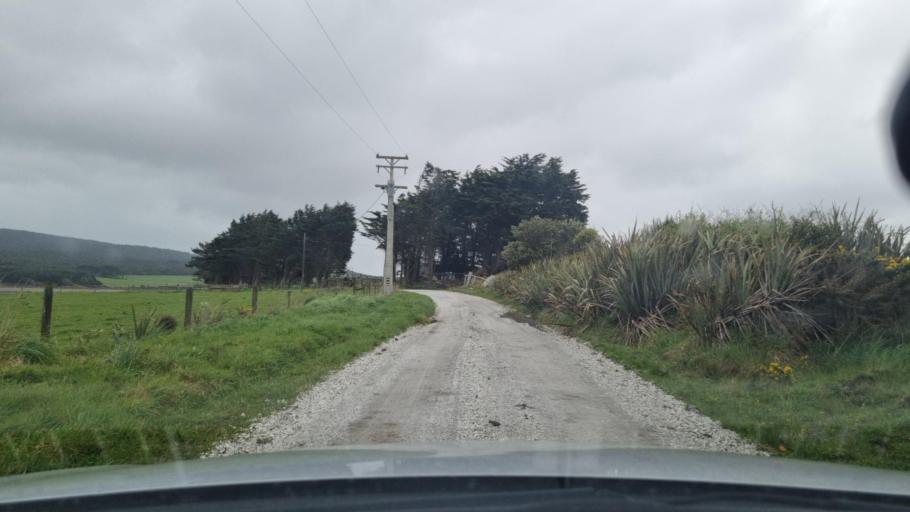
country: NZ
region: Southland
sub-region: Invercargill City
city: Bluff
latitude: -46.5384
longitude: 168.2900
